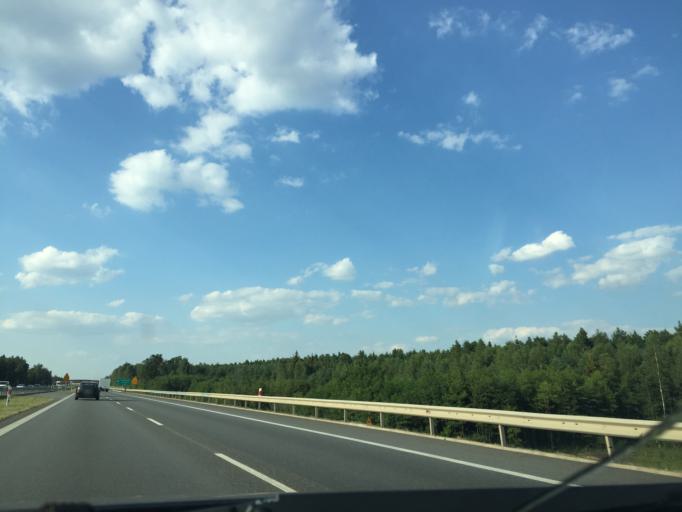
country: PL
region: Masovian Voivodeship
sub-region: Powiat szydlowiecki
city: Szydlowiec
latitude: 51.1722
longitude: 20.8592
